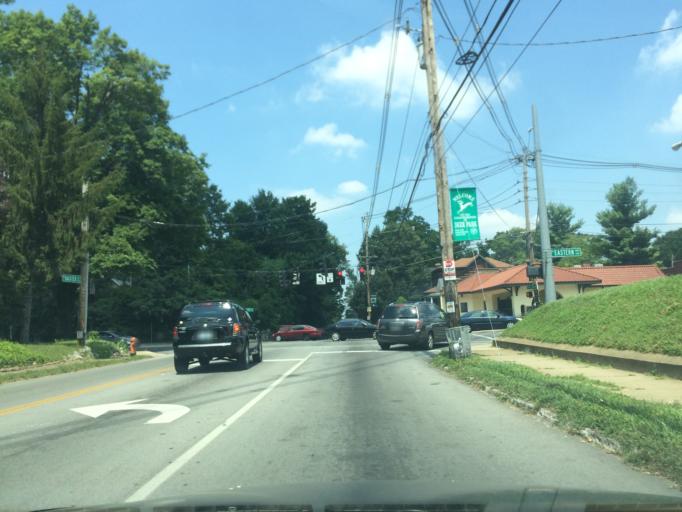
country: US
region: Kentucky
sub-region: Jefferson County
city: Audubon Park
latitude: 38.2285
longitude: -85.7149
